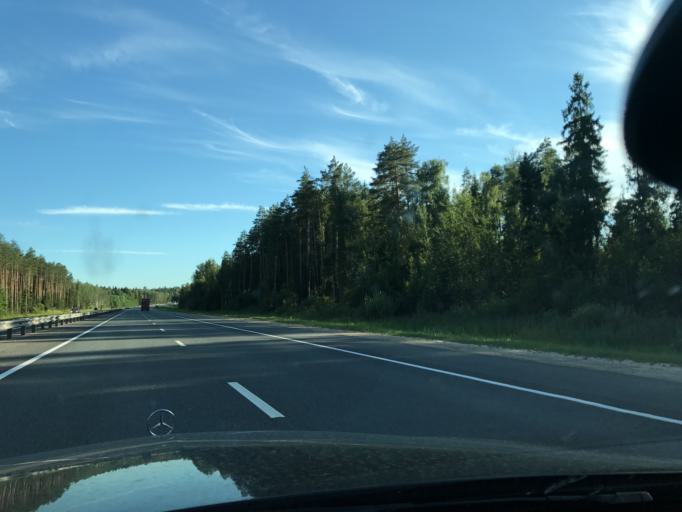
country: RU
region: Vladimir
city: Kameshkovo
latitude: 56.1821
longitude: 40.9477
